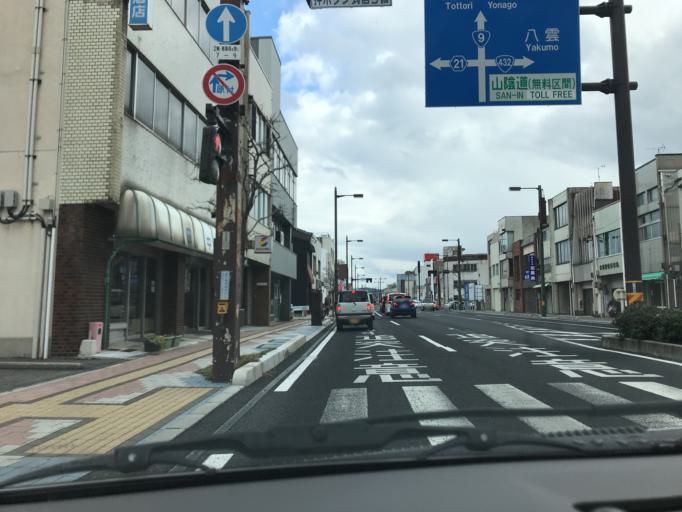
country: JP
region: Shimane
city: Matsue-shi
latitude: 35.4590
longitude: 133.0595
